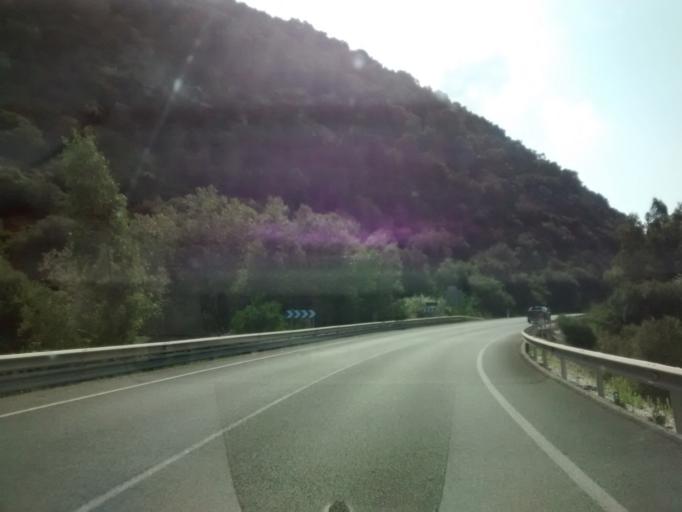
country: ES
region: Andalusia
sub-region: Provincia de Cadiz
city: Vejer de la Frontera
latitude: 36.2581
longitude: -5.9586
